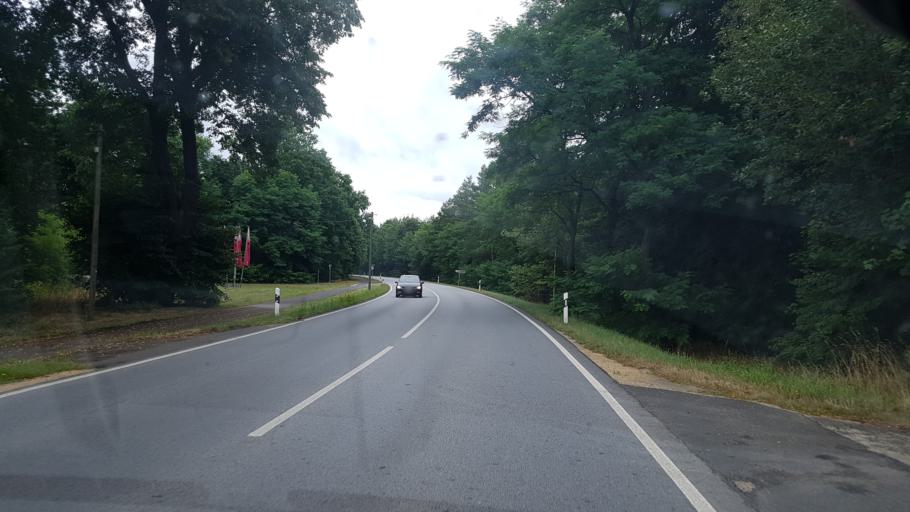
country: DE
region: Saxony
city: Niesky
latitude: 51.2714
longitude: 14.8160
